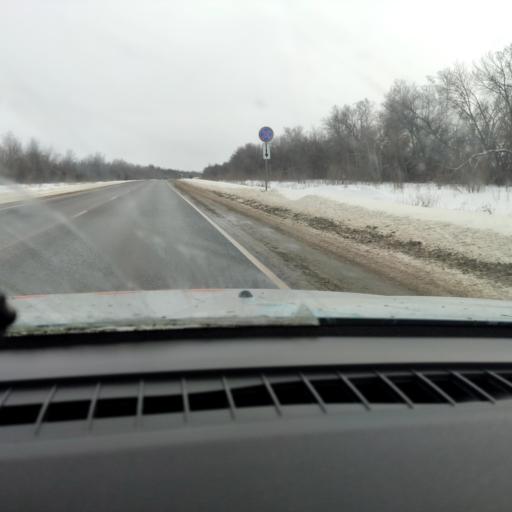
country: RU
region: Samara
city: Dubovyy Umet
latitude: 53.0044
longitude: 50.2483
